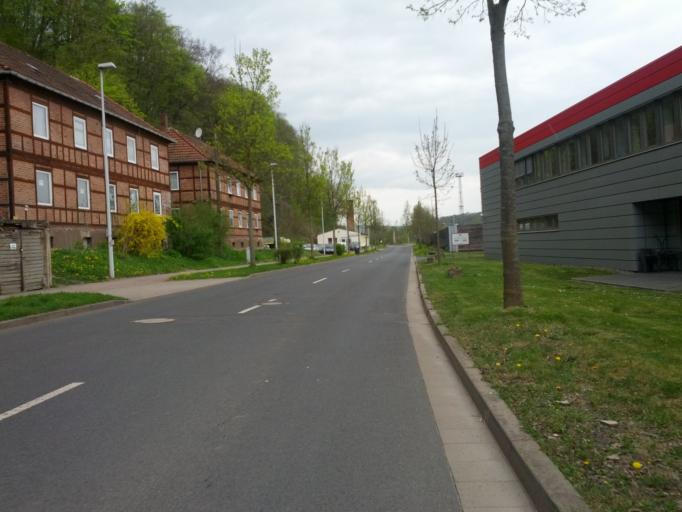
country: DE
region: Thuringia
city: Eisenach
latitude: 50.9690
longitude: 10.3440
